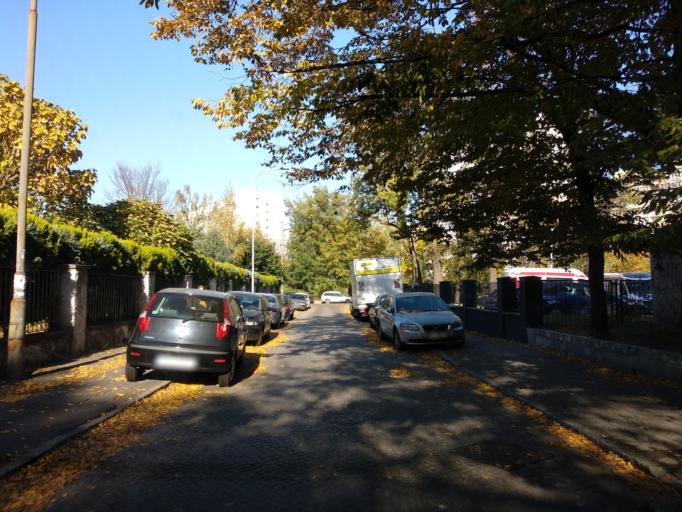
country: PL
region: Lower Silesian Voivodeship
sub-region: Powiat wroclawski
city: Wroclaw
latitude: 51.0930
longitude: 17.0109
